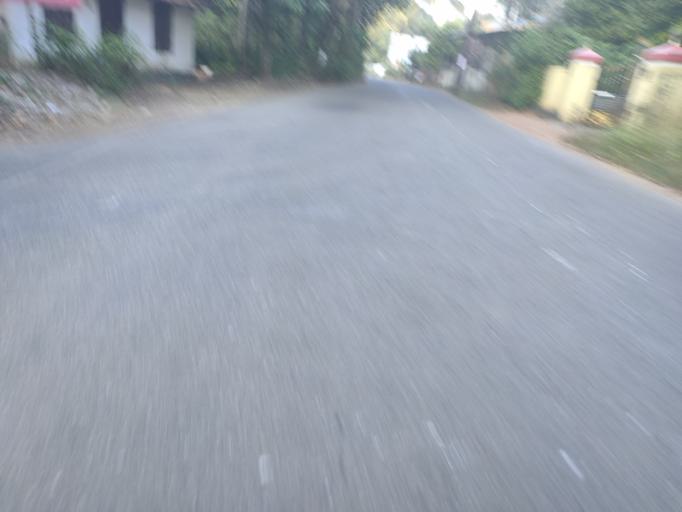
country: IN
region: Kerala
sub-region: Thrissur District
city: Kizhake Chalakudi
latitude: 10.2279
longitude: 76.3288
